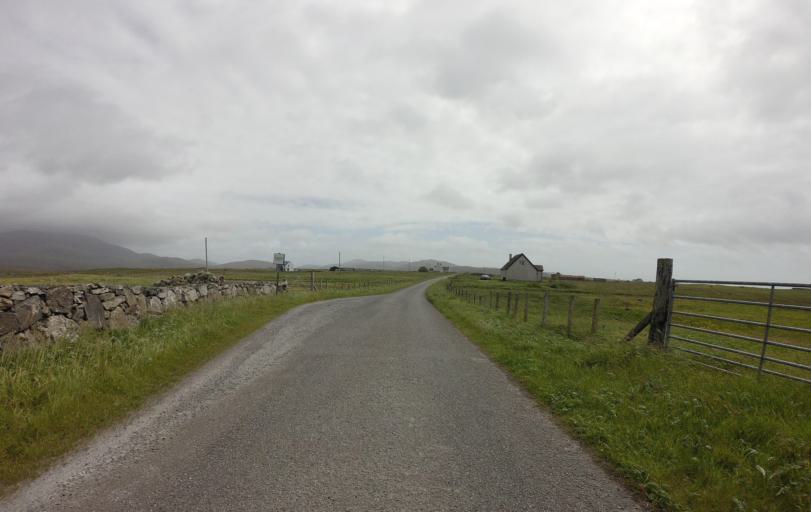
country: GB
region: Scotland
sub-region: Eilean Siar
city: Isle of South Uist
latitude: 57.2603
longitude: -7.4068
